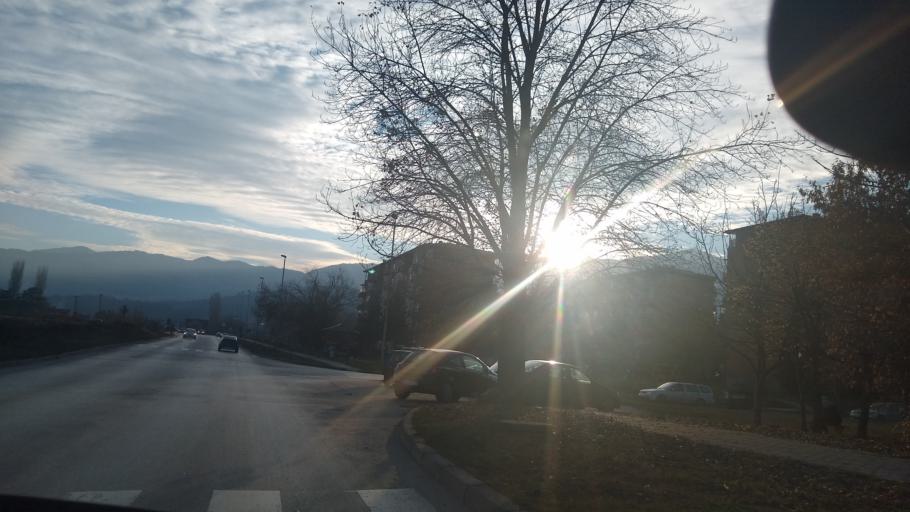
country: MK
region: Bitola
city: Bitola
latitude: 41.0284
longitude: 21.3465
